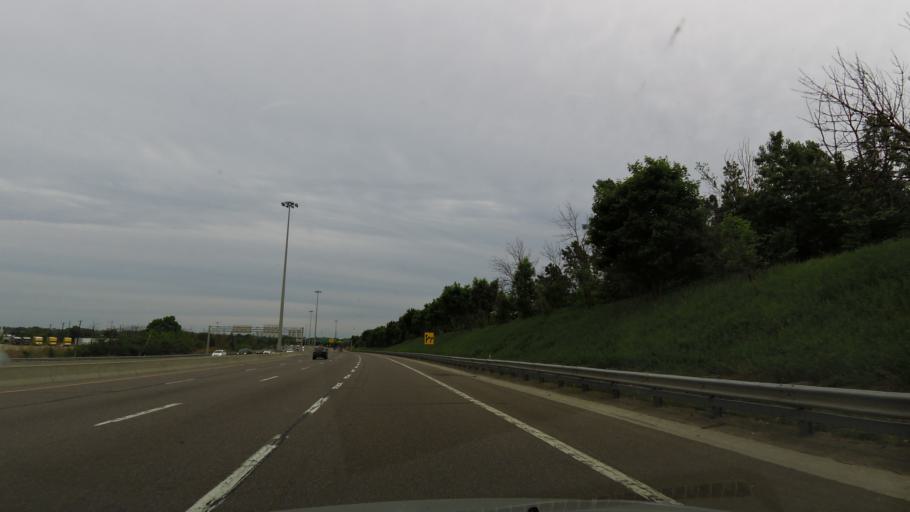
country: CA
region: Ontario
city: Etobicoke
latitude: 43.7129
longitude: -79.5138
